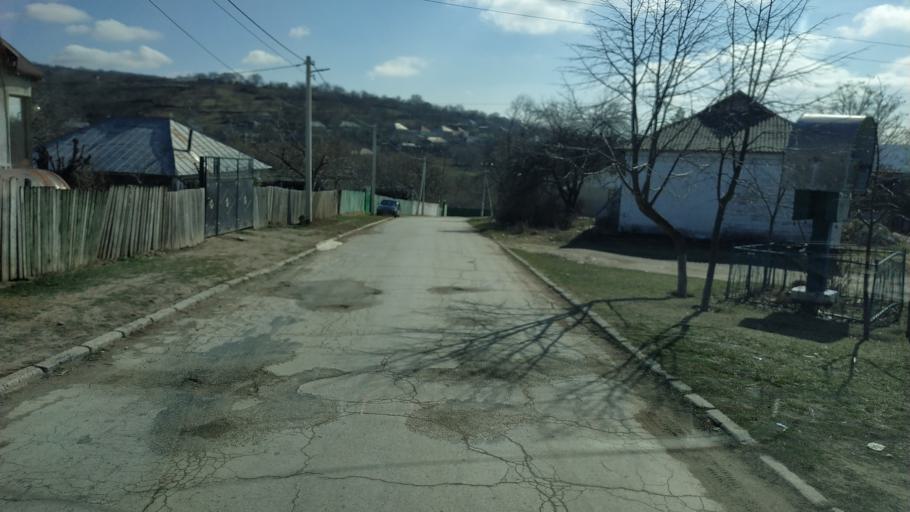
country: MD
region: Straseni
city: Straseni
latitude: 47.0192
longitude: 28.5438
